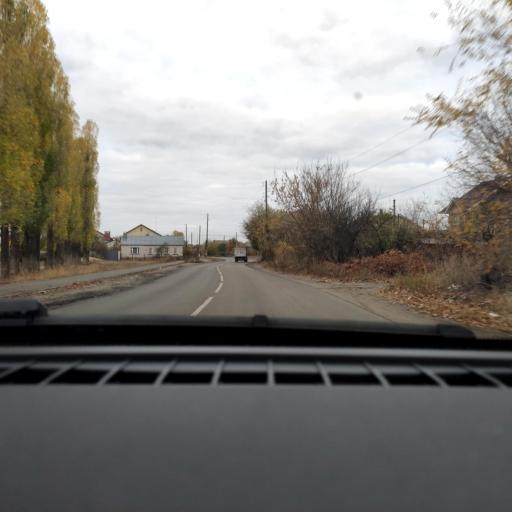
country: RU
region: Voronezj
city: Somovo
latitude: 51.7344
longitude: 39.2781
